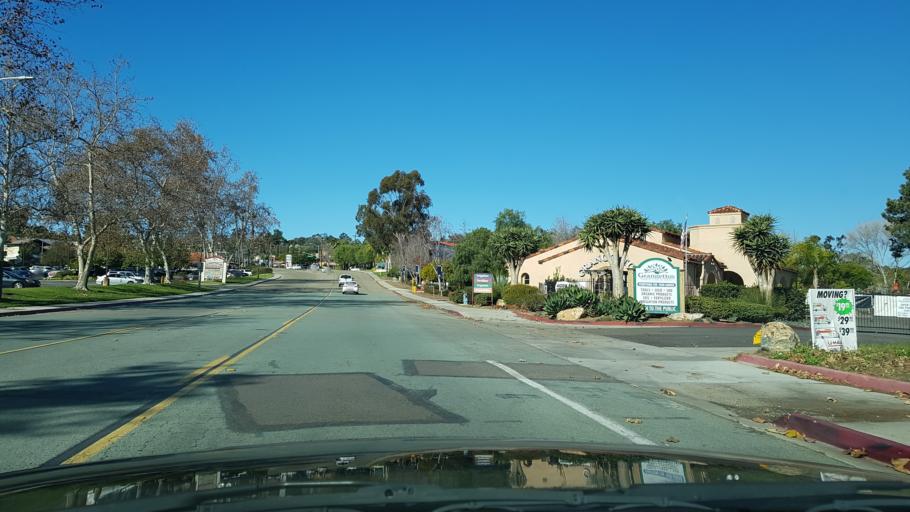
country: US
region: California
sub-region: San Diego County
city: Rancho Santa Fe
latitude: 33.0350
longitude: -117.2370
